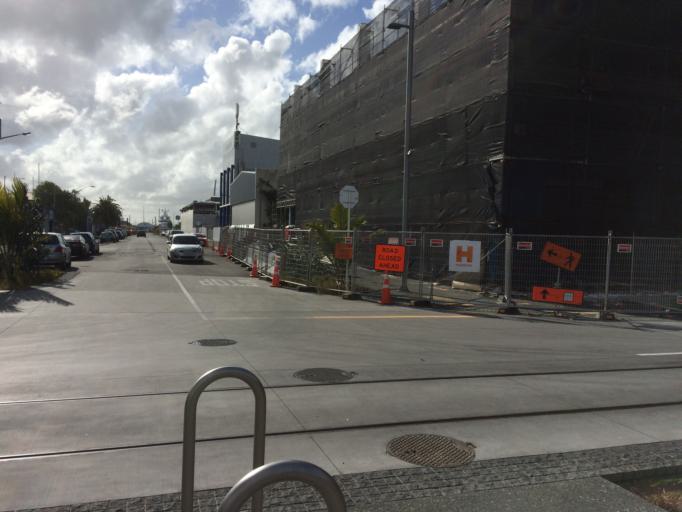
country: NZ
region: Auckland
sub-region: Auckland
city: Auckland
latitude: -36.8424
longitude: 174.7579
